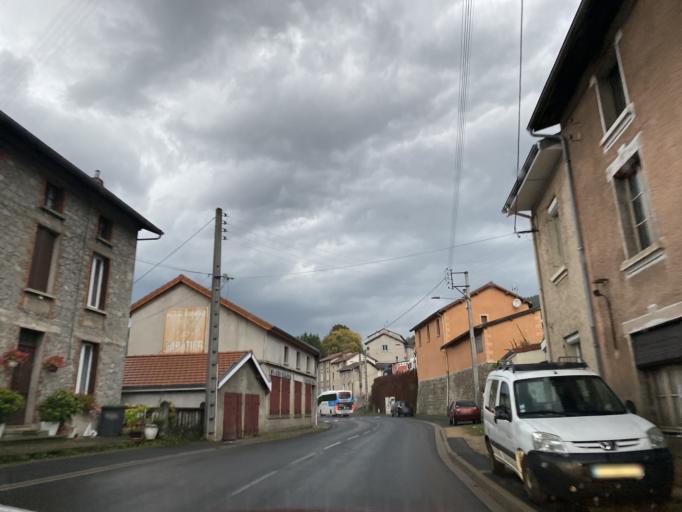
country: FR
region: Auvergne
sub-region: Departement du Puy-de-Dome
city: Celles-sur-Durolle
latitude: 45.8668
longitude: 3.6209
